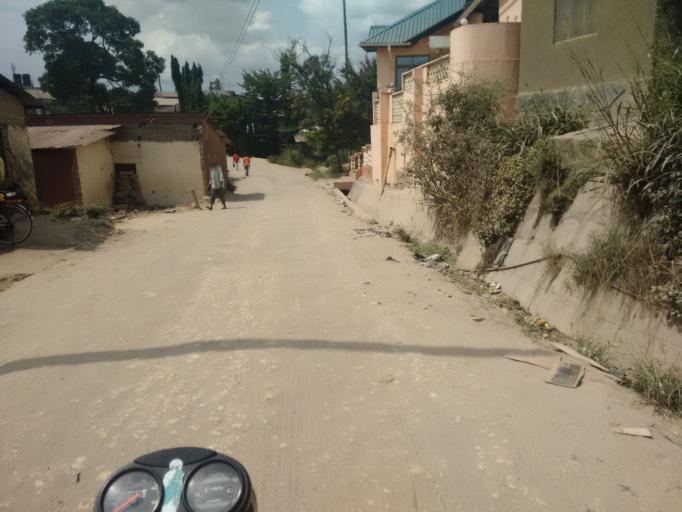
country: TZ
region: Dar es Salaam
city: Dar es Salaam
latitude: -6.8572
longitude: 39.2435
